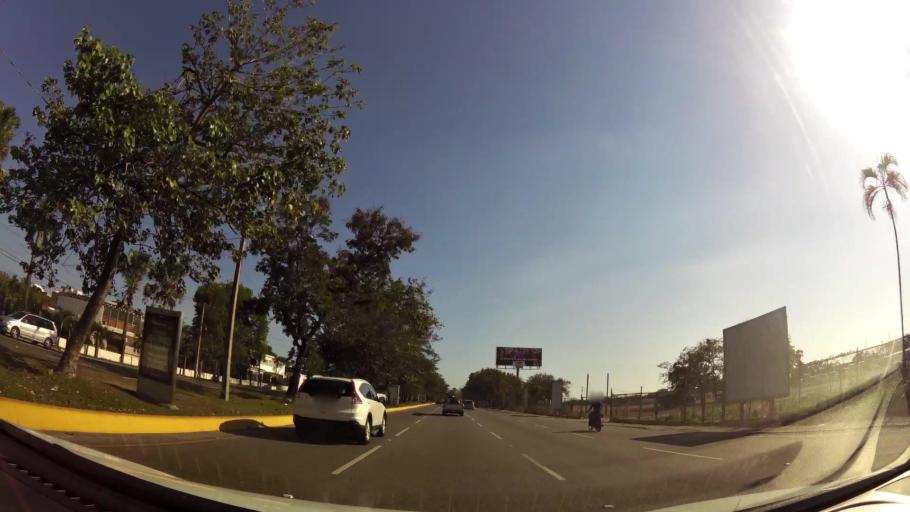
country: DO
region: Nacional
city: Bella Vista
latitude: 18.4730
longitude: -69.9682
